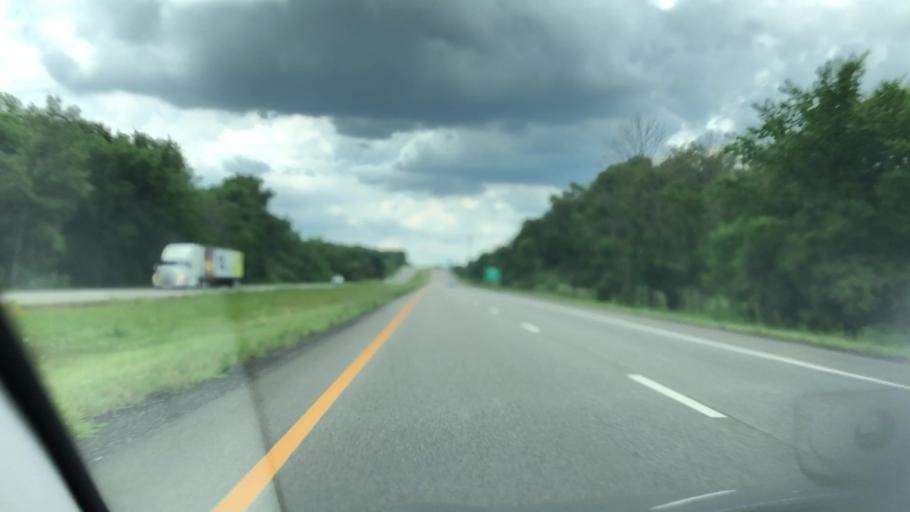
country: US
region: Ohio
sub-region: Summit County
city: Norton
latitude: 41.0887
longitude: -81.6605
